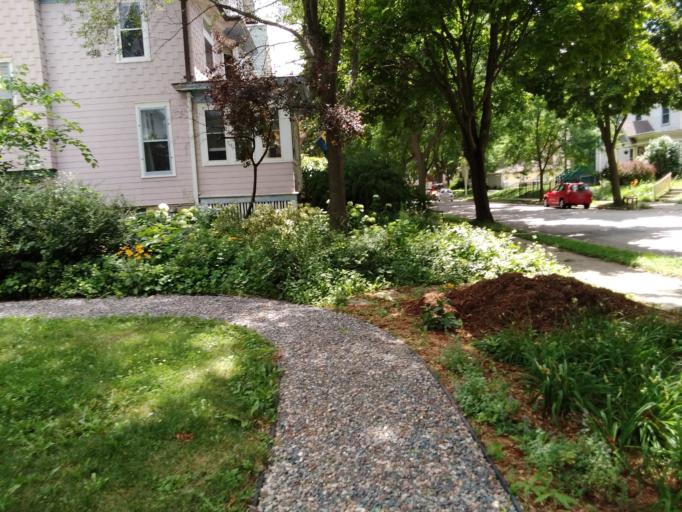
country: US
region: Wisconsin
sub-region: Milwaukee County
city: West Milwaukee
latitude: 43.0470
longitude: -87.9487
